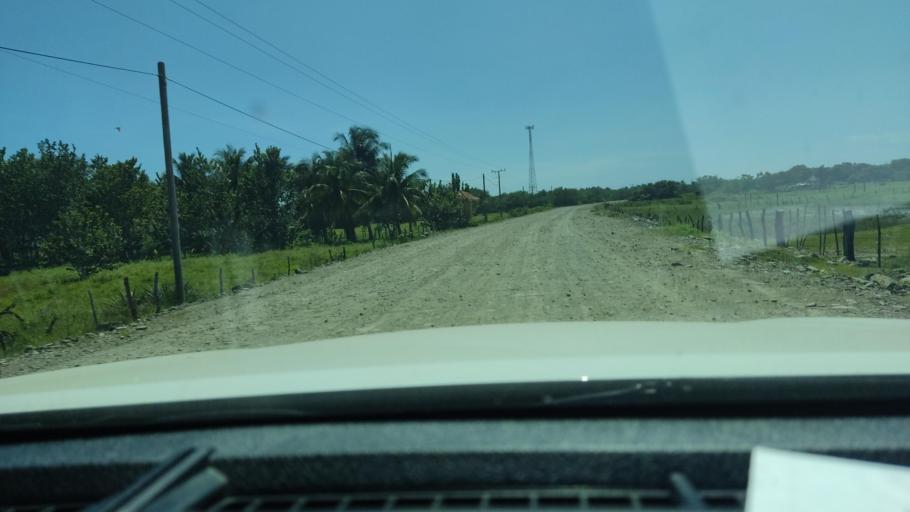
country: SV
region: Ahuachapan
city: San Francisco Menendez
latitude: 13.7673
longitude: -90.1782
